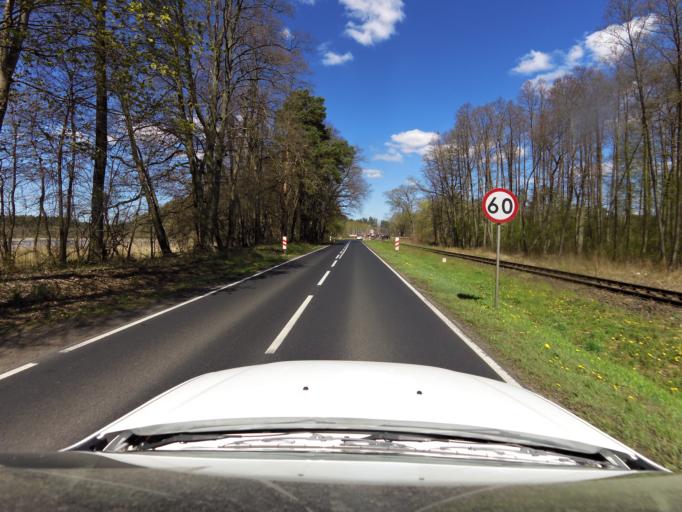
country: PL
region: West Pomeranian Voivodeship
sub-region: Powiat mysliborski
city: Debno
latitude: 52.7665
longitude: 14.7394
